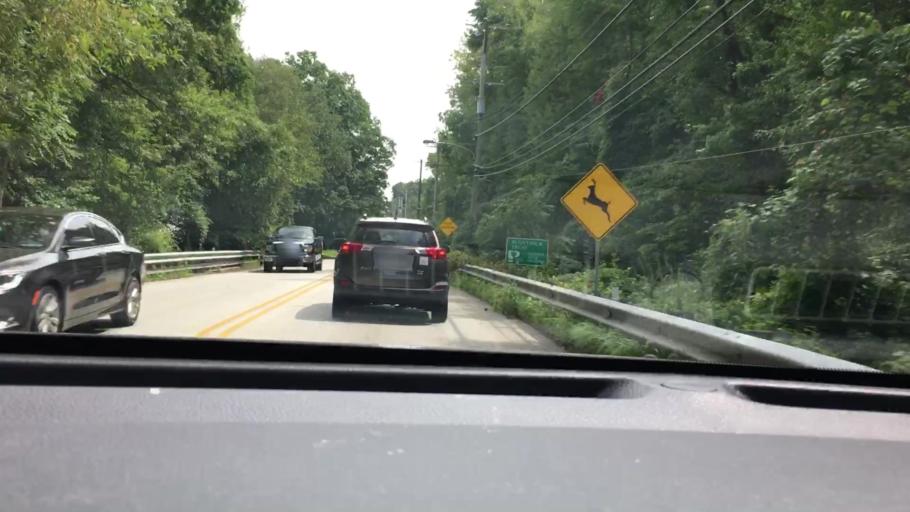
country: US
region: Pennsylvania
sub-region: Bucks County
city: Warminster Heights
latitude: 40.1598
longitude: -75.0763
